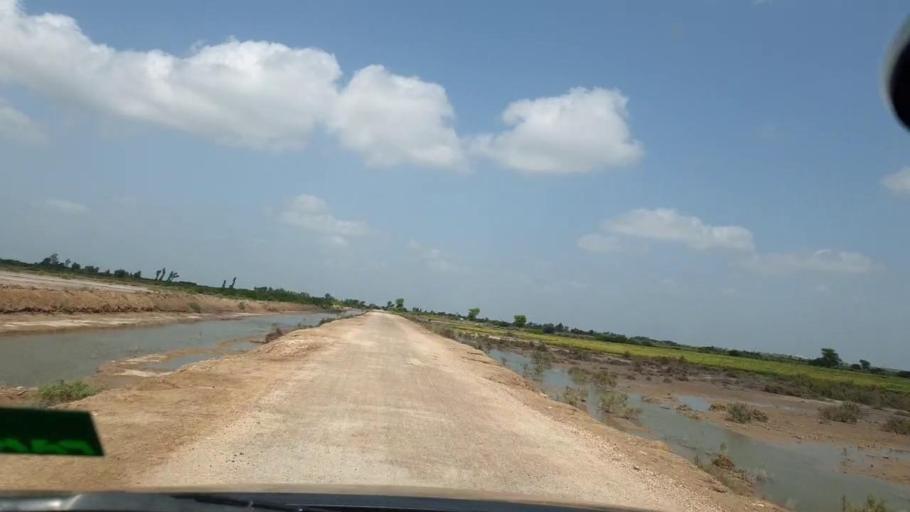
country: PK
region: Sindh
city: Kadhan
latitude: 24.5990
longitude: 69.1261
